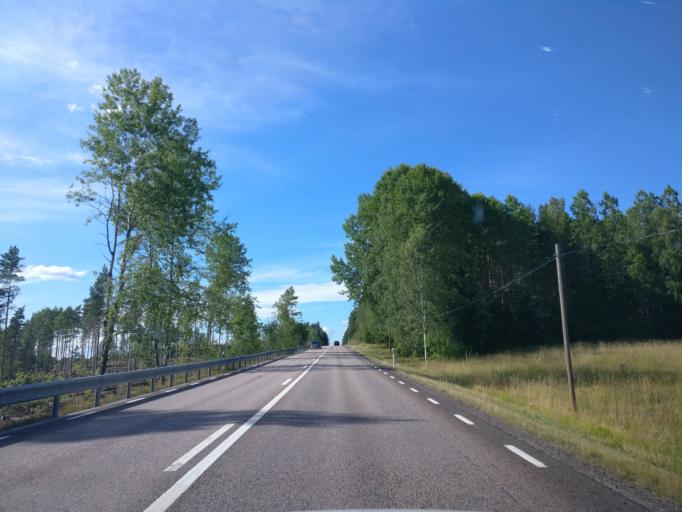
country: SE
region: Vaermland
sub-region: Karlstads Kommun
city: Edsvalla
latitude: 59.5828
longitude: 13.0155
